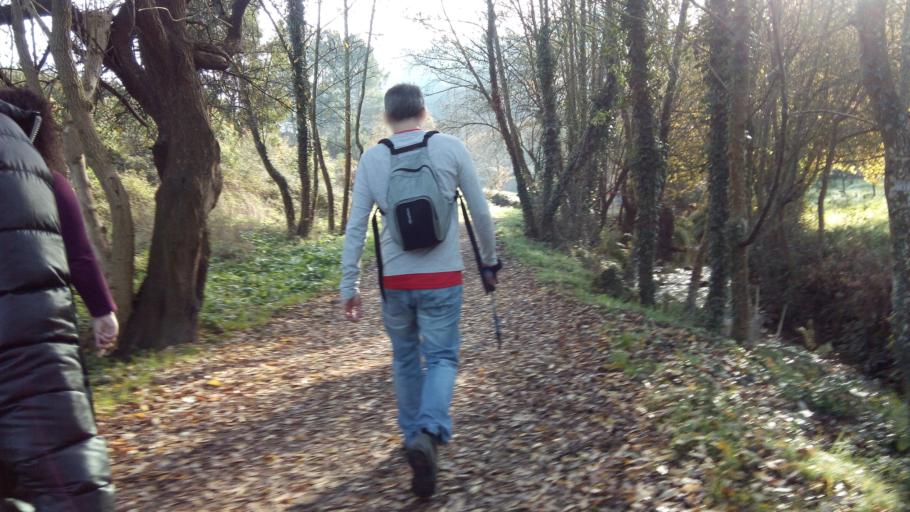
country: ES
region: Galicia
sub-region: Provincia de Pontevedra
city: Meis
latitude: 42.4922
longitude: -8.7571
